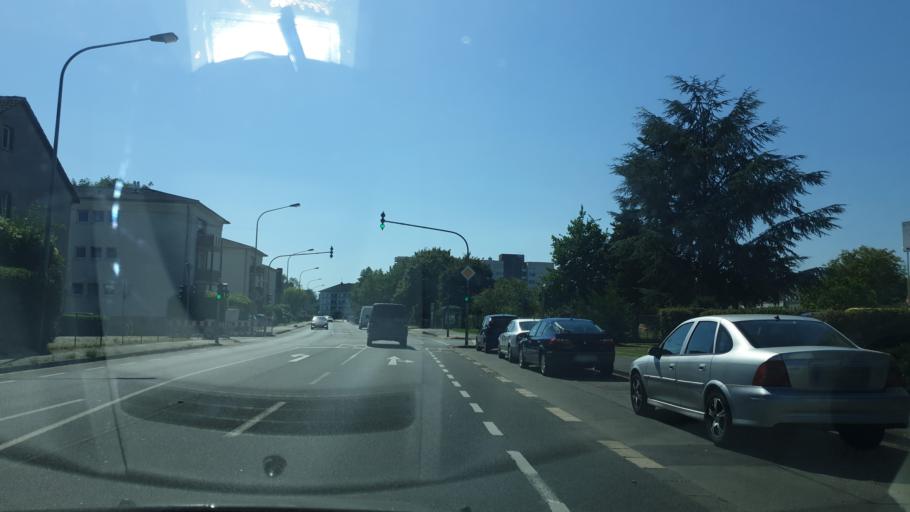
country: DE
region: North Rhine-Westphalia
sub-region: Regierungsbezirk Koln
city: Euskirchen
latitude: 50.6658
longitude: 6.7758
